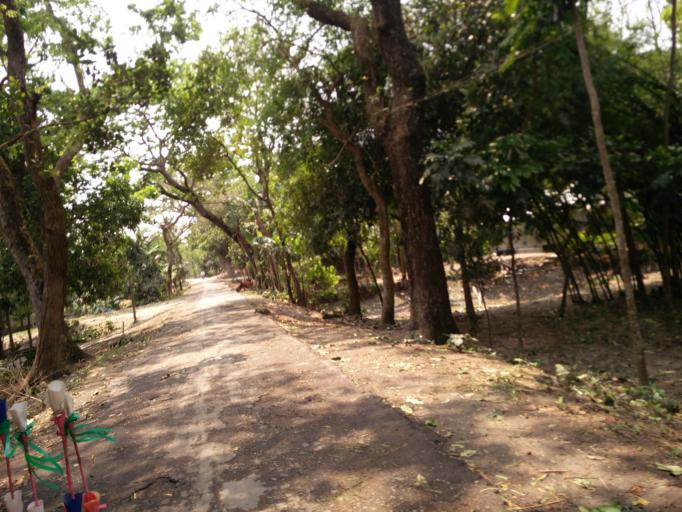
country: BD
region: Dhaka
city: Sherpur
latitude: 24.9487
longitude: 90.1613
